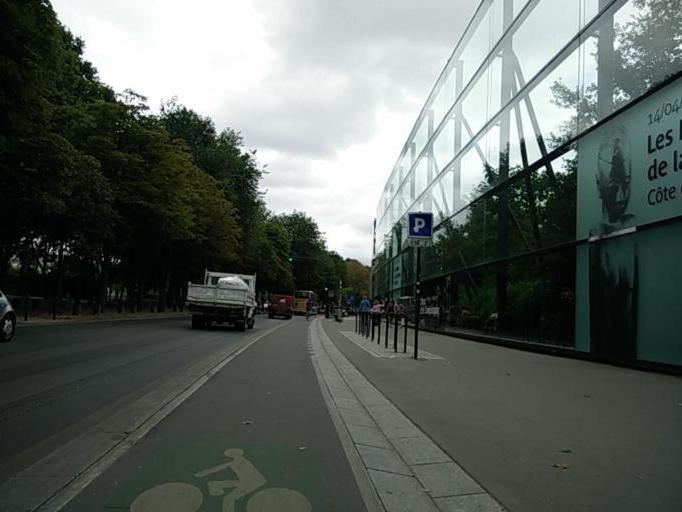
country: FR
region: Ile-de-France
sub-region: Departement des Hauts-de-Seine
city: Levallois-Perret
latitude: 48.8612
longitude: 2.2969
